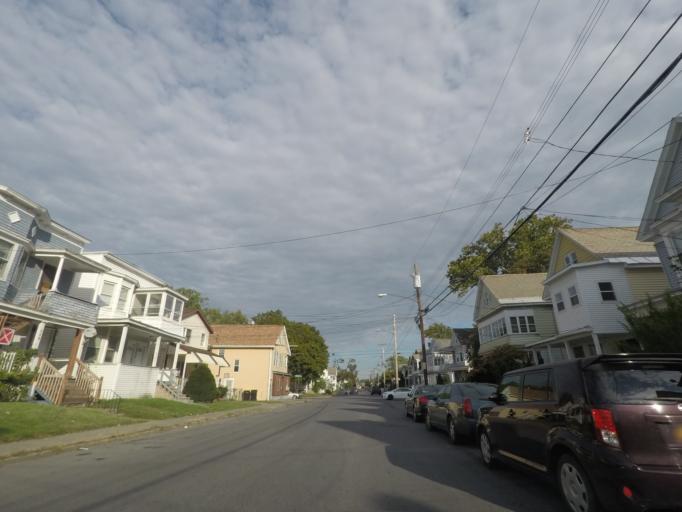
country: US
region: New York
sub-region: Albany County
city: Albany
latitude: 42.6394
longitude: -73.7823
